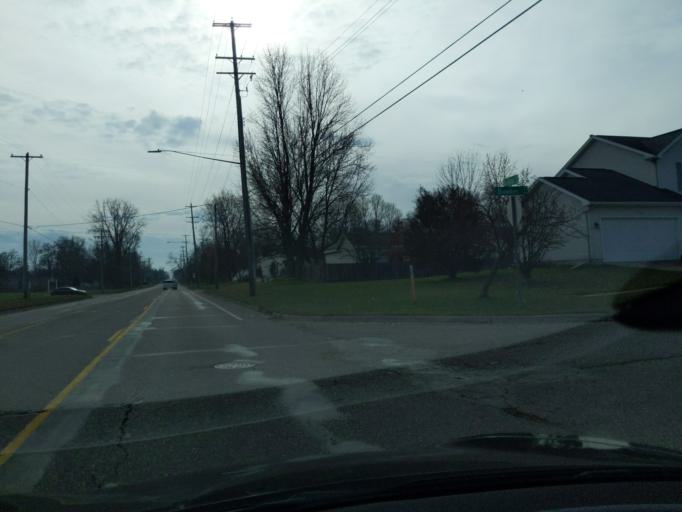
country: US
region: Michigan
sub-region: Ingham County
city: Holt
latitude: 42.6607
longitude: -84.5236
